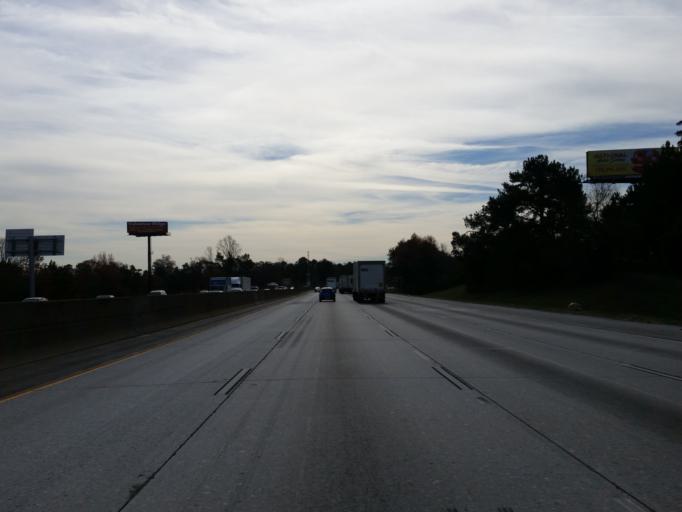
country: US
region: Georgia
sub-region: Cobb County
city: Vinings
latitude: 33.8342
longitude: -84.4866
